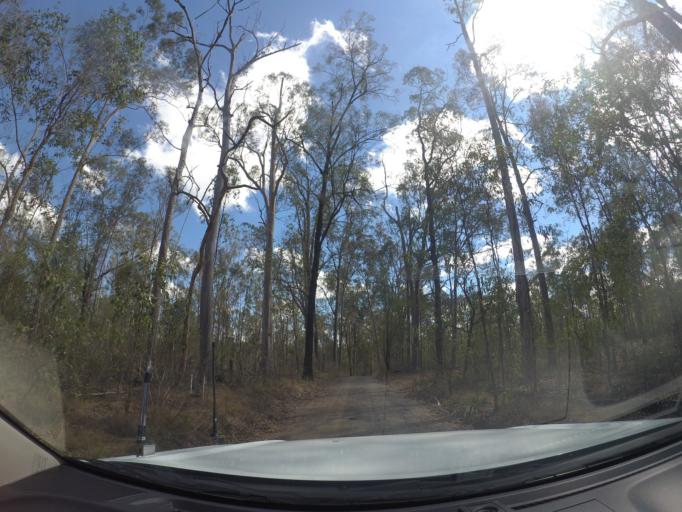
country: AU
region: Queensland
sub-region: Logan
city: Cedar Vale
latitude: -27.8361
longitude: 152.9665
